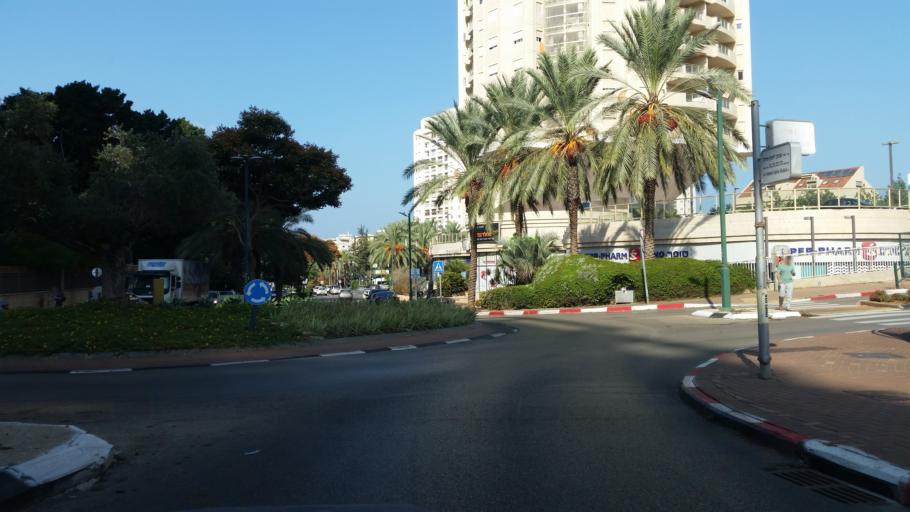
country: IL
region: Tel Aviv
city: Ramat HaSharon
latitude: 32.1510
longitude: 34.8436
